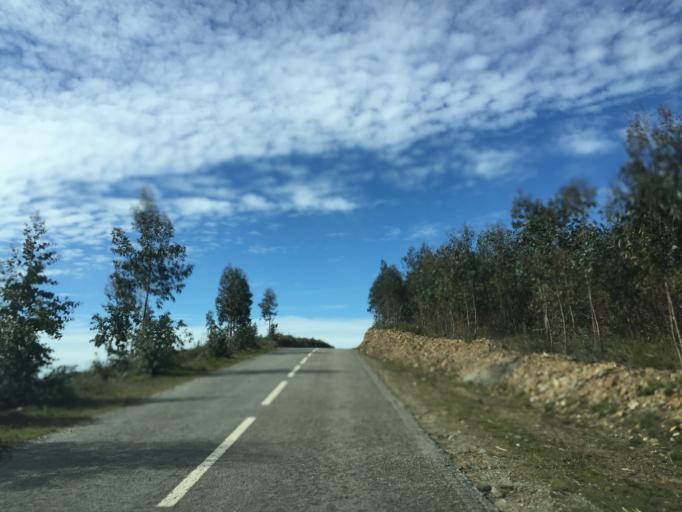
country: PT
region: Aveiro
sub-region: Arouca
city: Arouca
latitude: 40.9598
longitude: -8.2323
